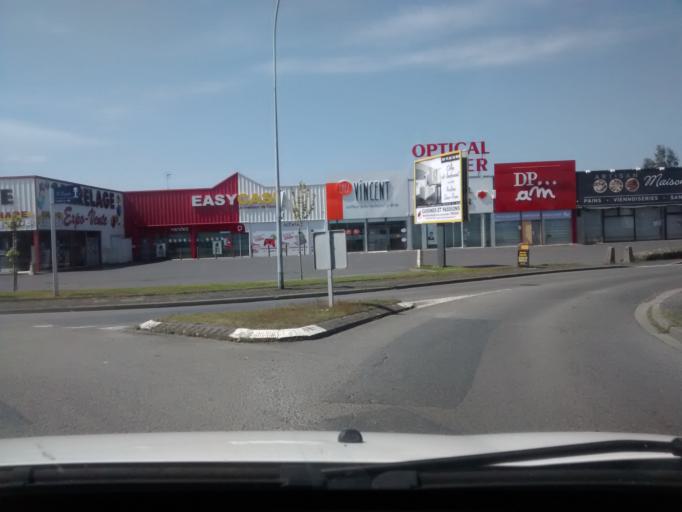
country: FR
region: Brittany
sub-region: Departement des Cotes-d'Armor
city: Langueux
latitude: 48.4970
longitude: -2.7321
